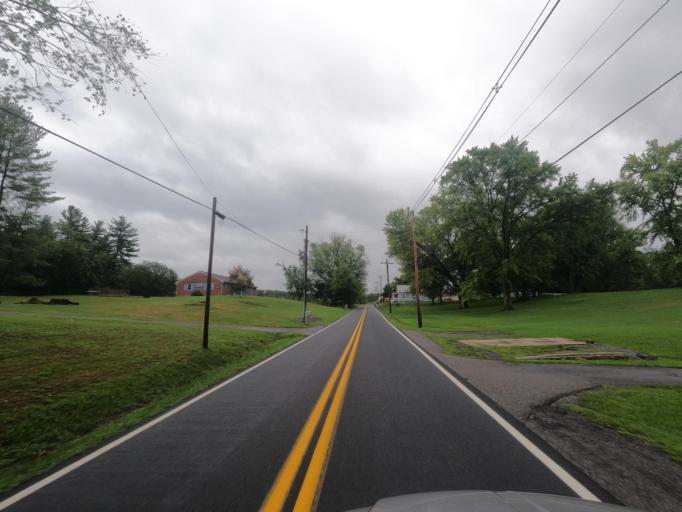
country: US
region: West Virginia
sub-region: Berkeley County
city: Martinsburg
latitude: 39.6219
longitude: -78.0140
